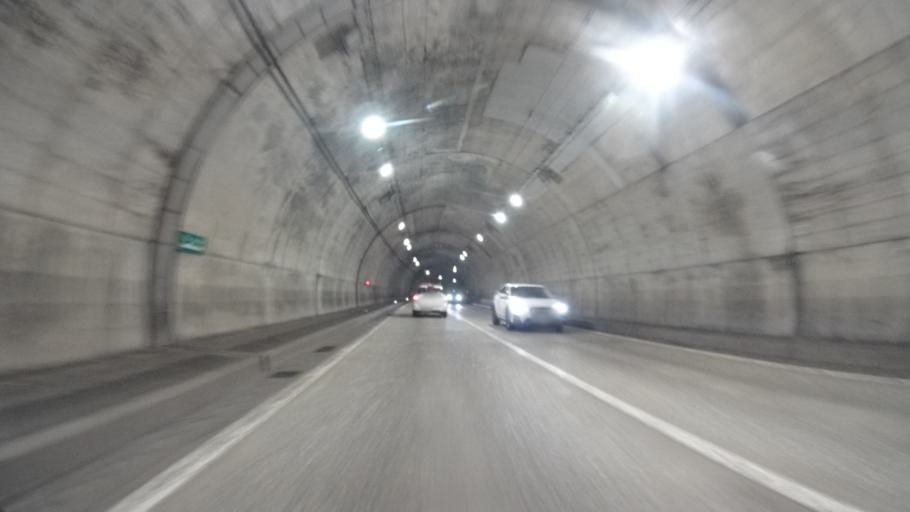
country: JP
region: Niigata
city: Kashiwazaki
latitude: 37.4084
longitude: 138.6611
